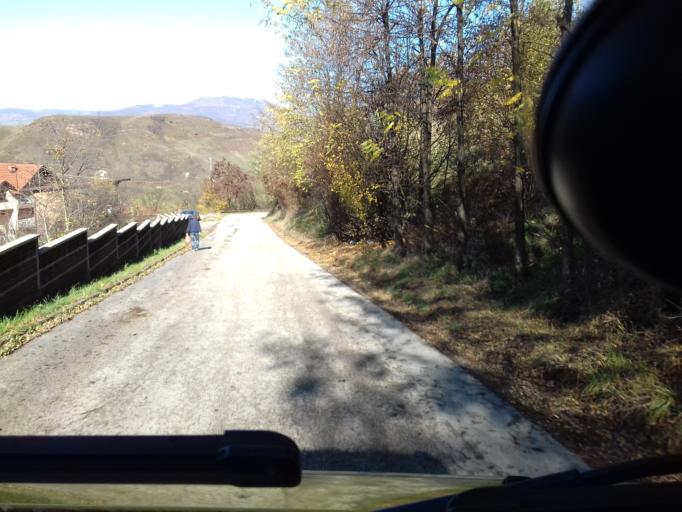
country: BA
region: Federation of Bosnia and Herzegovina
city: Zenica
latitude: 44.1789
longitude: 17.9061
